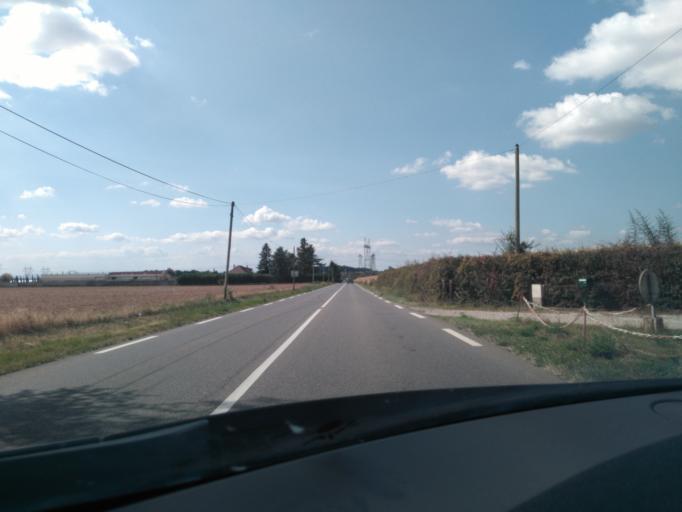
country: FR
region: Rhone-Alpes
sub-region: Departement du Rhone
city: Saint-Bonnet-de-Mure
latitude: 45.7244
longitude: 5.0387
